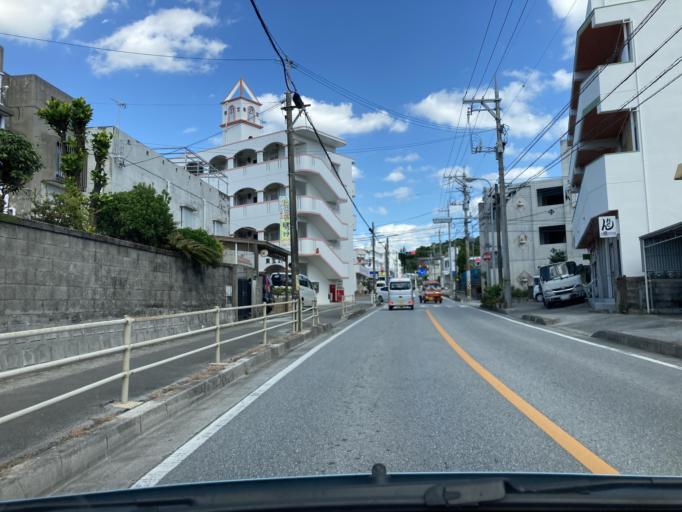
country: JP
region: Okinawa
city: Tomigusuku
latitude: 26.1882
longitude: 127.7282
